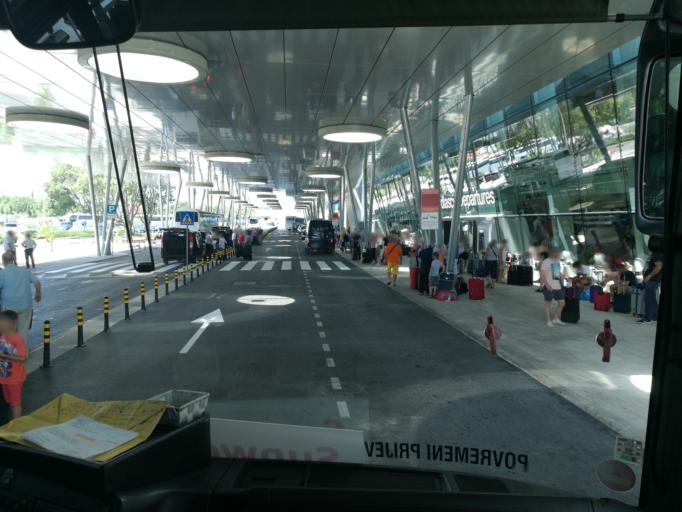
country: HR
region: Dubrovacko-Neretvanska
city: Jasenice
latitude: 42.5599
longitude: 18.2630
